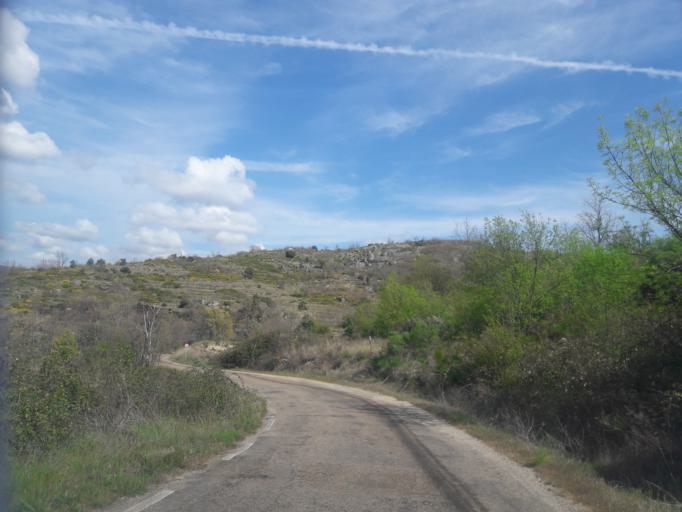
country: ES
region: Castille and Leon
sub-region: Provincia de Salamanca
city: San Esteban de la Sierra
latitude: 40.5083
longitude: -5.8859
